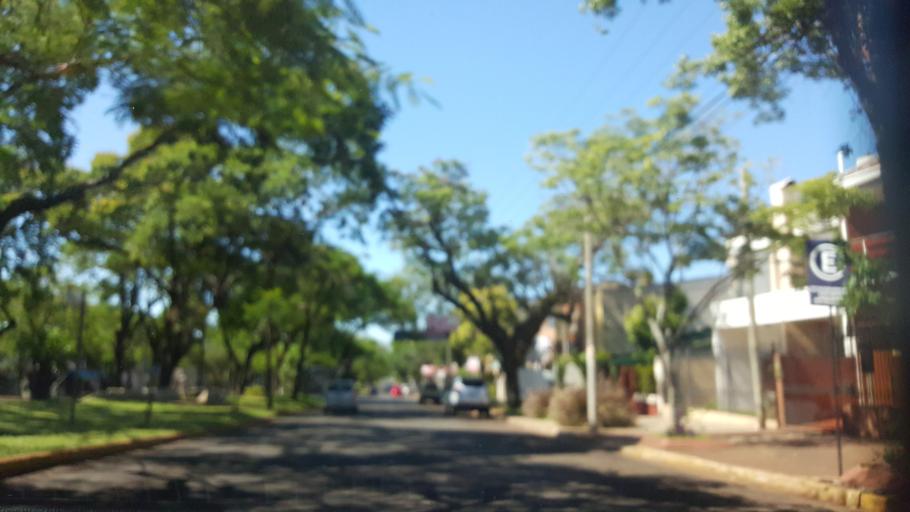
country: AR
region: Misiones
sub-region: Departamento de Capital
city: Posadas
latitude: -27.3718
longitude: -55.9018
